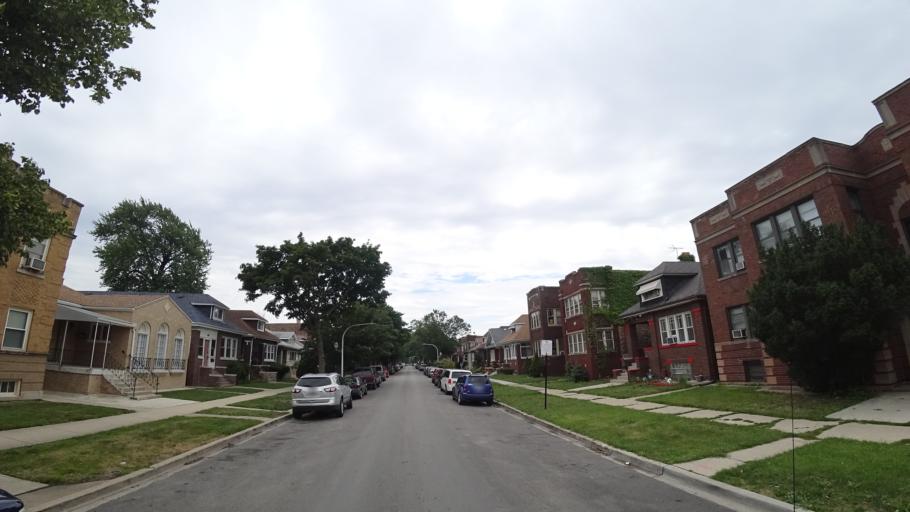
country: US
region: Illinois
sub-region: Cook County
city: Oak Park
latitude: 41.8691
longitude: -87.7730
